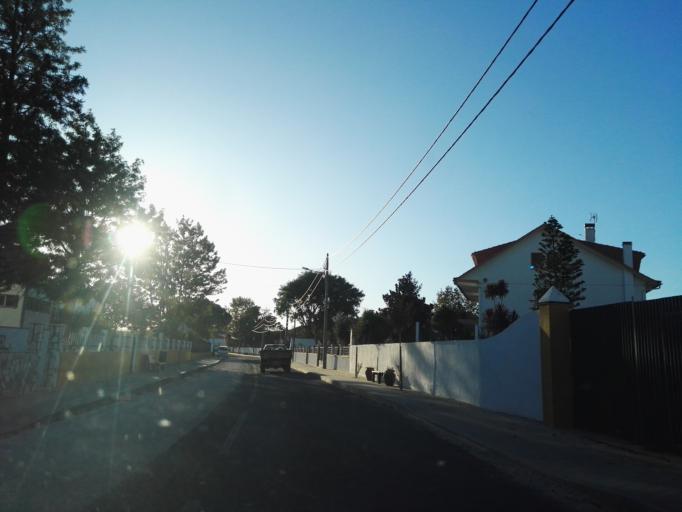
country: PT
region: Santarem
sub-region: Alpiarca
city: Alpiarca
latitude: 39.3425
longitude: -8.5521
